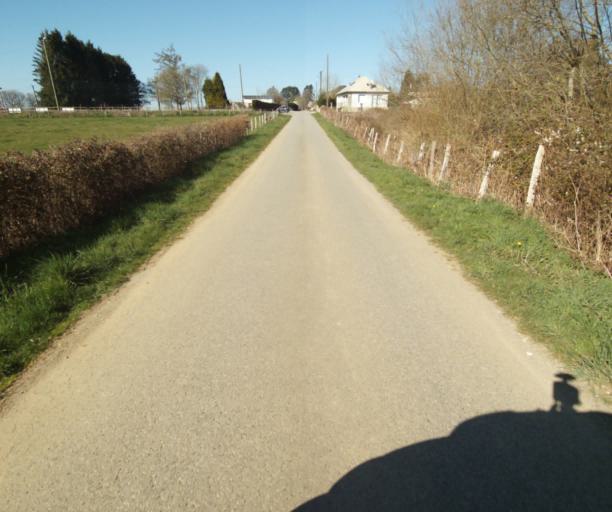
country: FR
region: Limousin
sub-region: Departement de la Correze
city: Chamboulive
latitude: 45.4679
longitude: 1.7338
